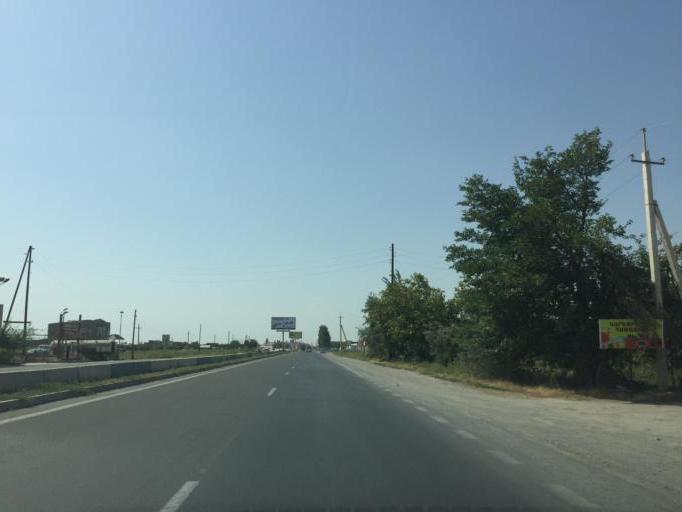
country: AM
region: Ararat
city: Artashat
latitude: 39.9522
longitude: 44.5404
